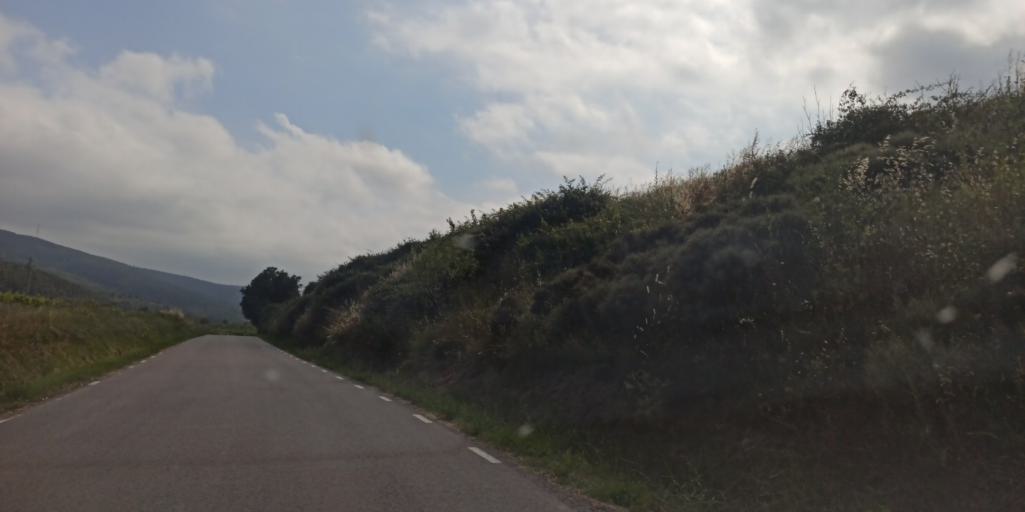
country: ES
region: Catalonia
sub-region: Provincia de Barcelona
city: Sant Joan de Mediona
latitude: 41.4727
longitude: 1.6008
